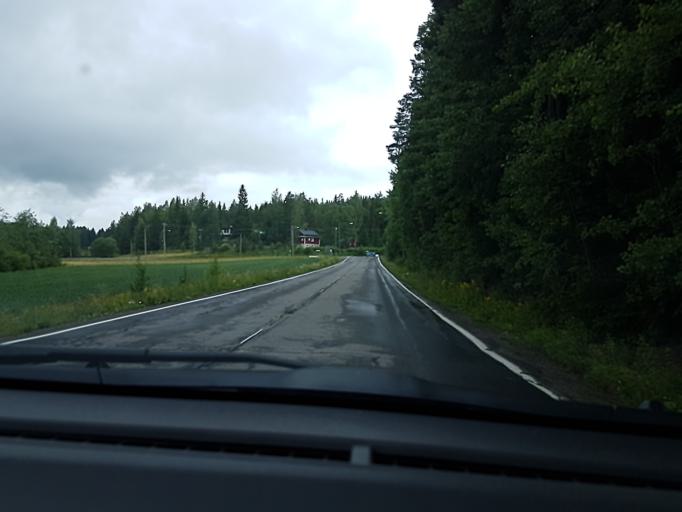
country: FI
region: Uusimaa
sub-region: Helsinki
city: Pornainen
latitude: 60.4392
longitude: 25.3792
